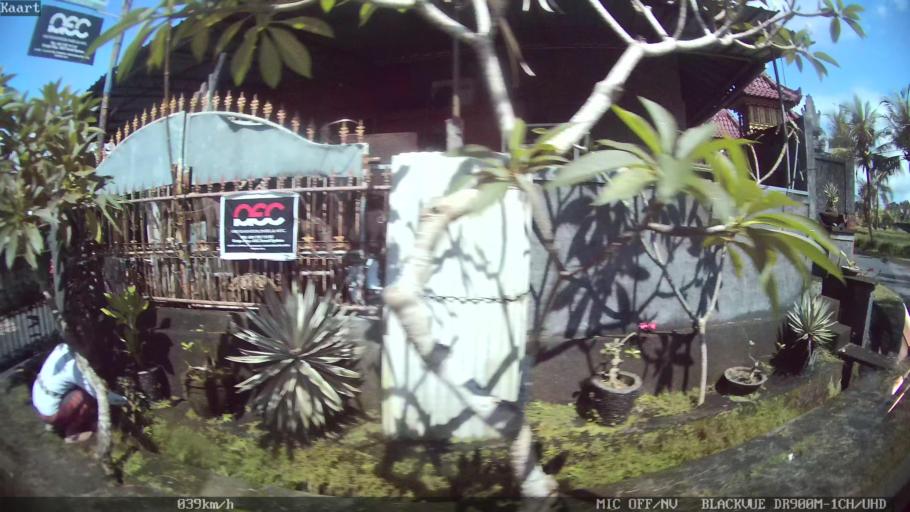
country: ID
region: Bali
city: Banjar Sedang
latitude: -8.5538
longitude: 115.2691
